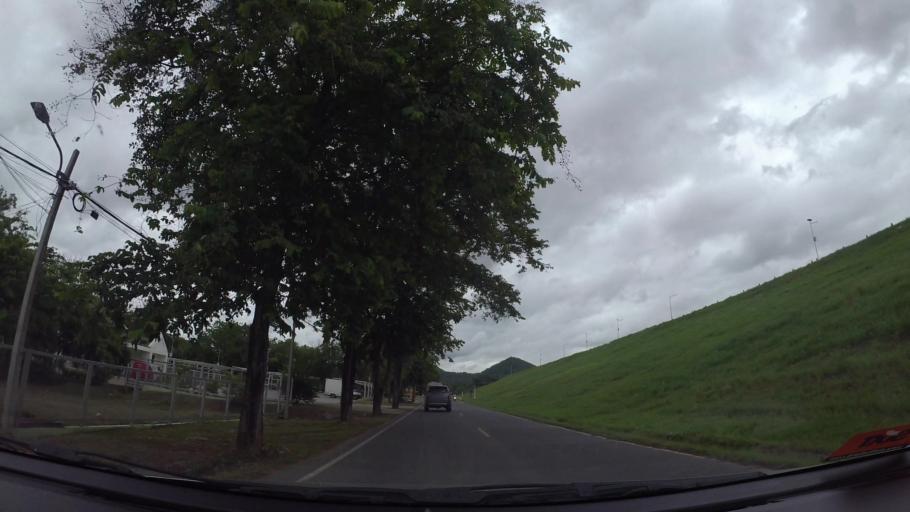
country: TH
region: Chon Buri
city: Si Racha
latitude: 13.2162
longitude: 100.9630
